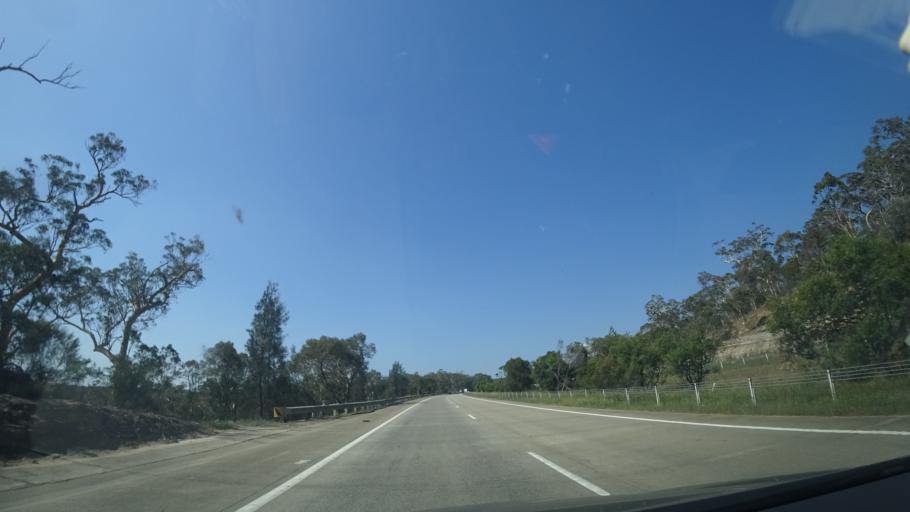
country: AU
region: New South Wales
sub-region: Wingecarribee
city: Moss Vale
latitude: -34.4798
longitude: 150.3157
